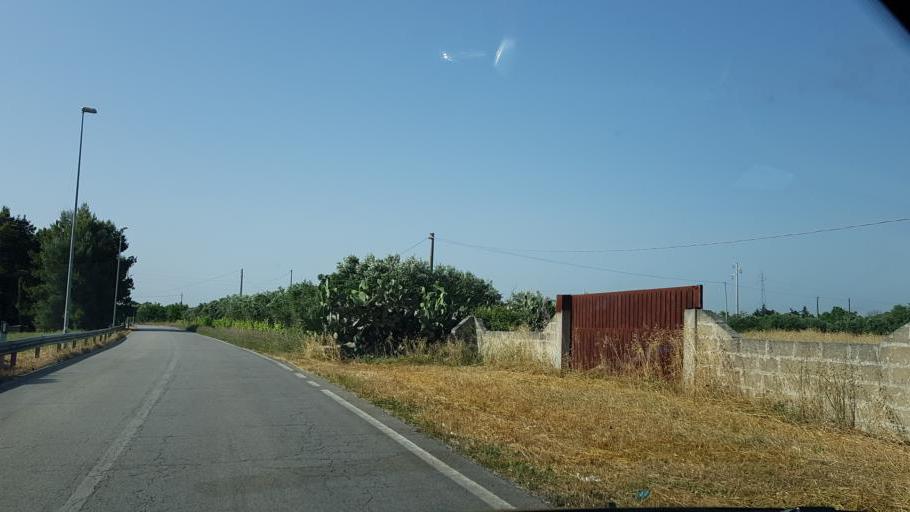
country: IT
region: Apulia
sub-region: Provincia di Brindisi
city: Mesagne
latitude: 40.5403
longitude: 17.8169
